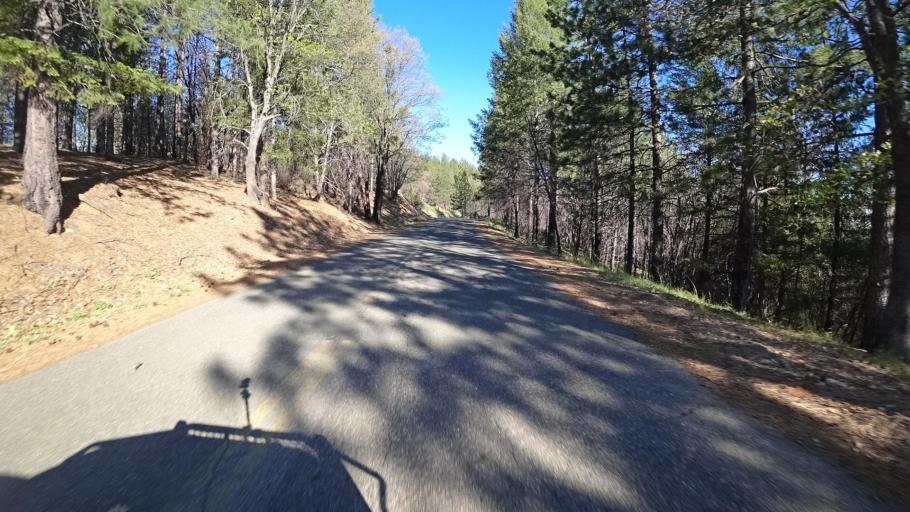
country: US
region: California
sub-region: Lake County
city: Upper Lake
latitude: 39.3126
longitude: -122.9443
